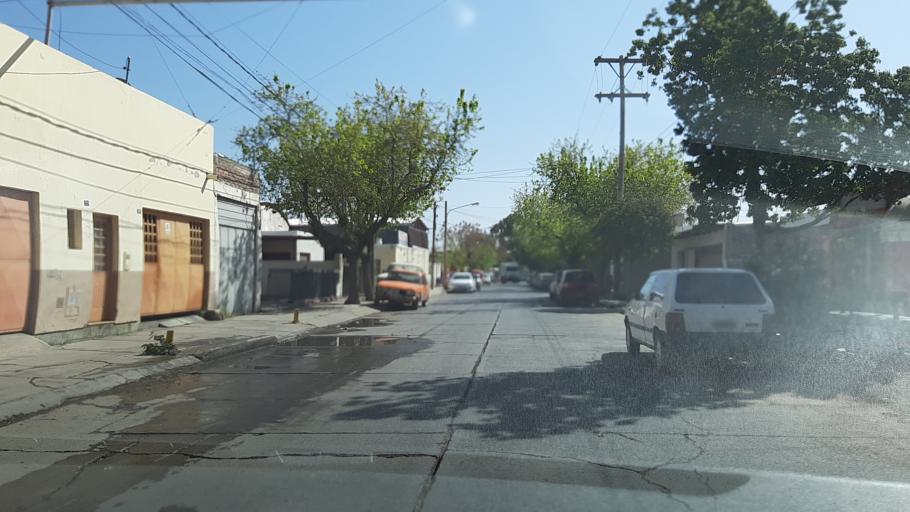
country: AR
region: San Juan
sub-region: Departamento de Santa Lucia
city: Santa Lucia
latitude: -31.5306
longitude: -68.5119
